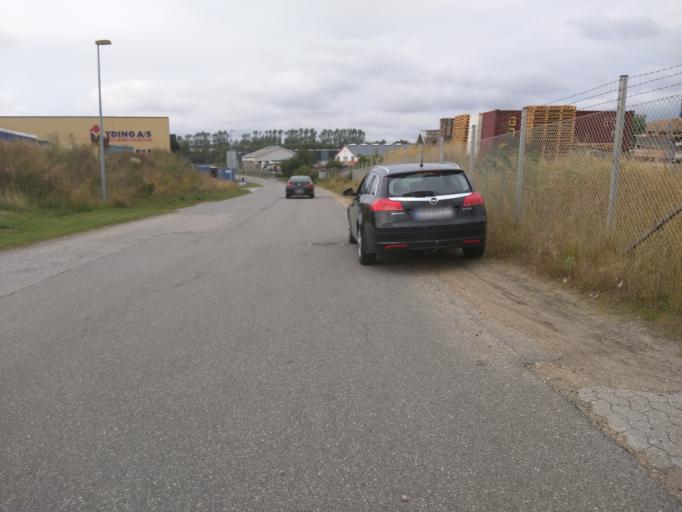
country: DK
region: Central Jutland
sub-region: Viborg Kommune
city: Viborg
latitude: 56.4513
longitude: 9.3648
